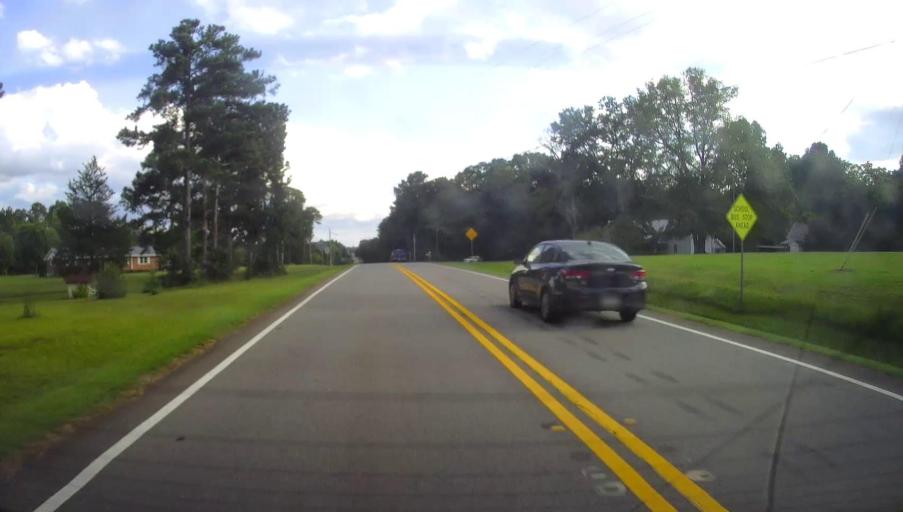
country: US
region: Georgia
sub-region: Monroe County
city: Forsyth
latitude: 32.9784
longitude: -83.9532
